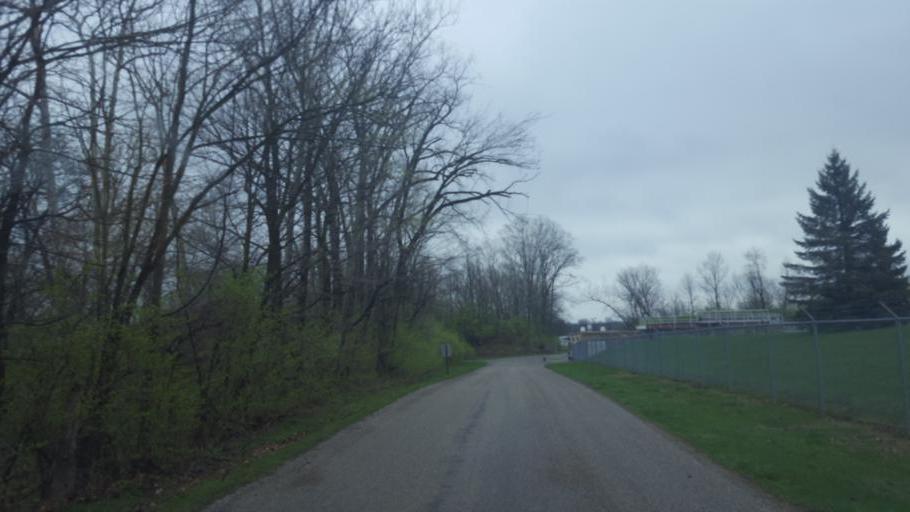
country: US
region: Ohio
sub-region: Morrow County
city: Mount Gilead
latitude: 40.5413
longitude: -82.8423
